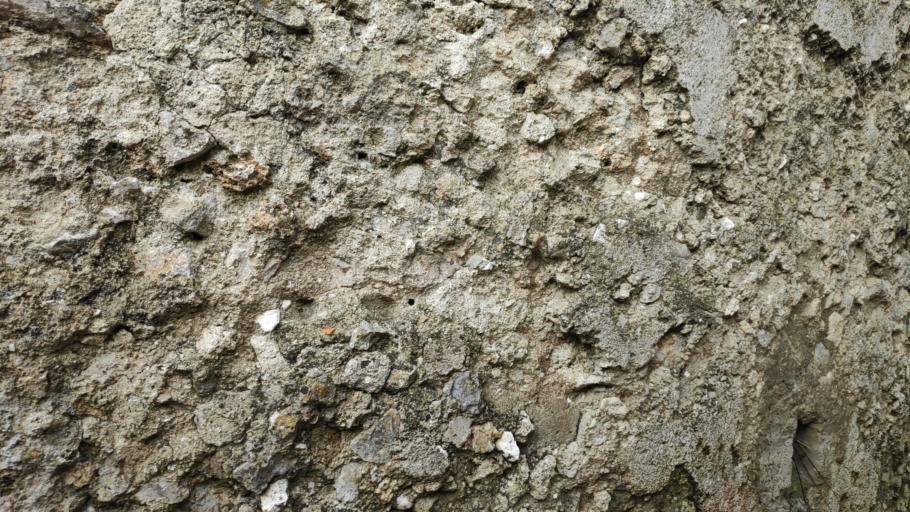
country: IT
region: Campania
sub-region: Provincia di Salerno
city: Ravello
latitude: 40.6472
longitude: 14.6111
